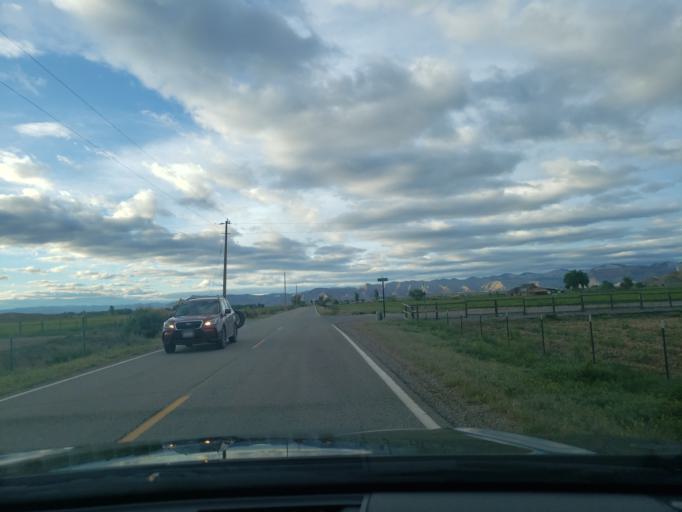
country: US
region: Colorado
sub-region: Mesa County
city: Fruita
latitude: 39.2217
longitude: -108.7197
